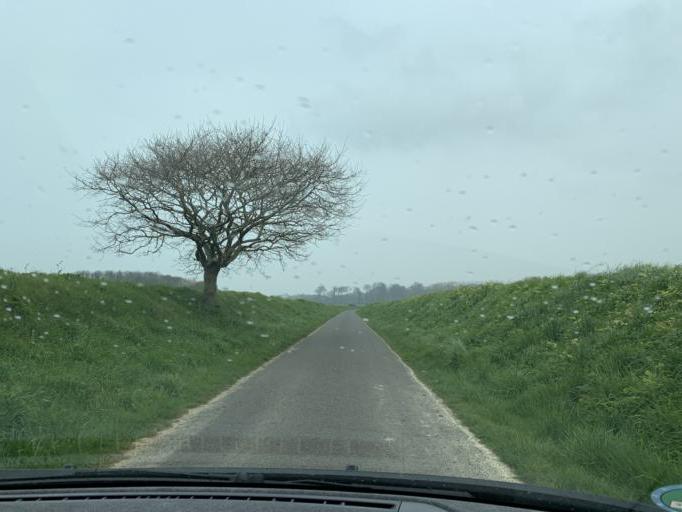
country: FR
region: Haute-Normandie
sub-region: Departement de la Seine-Maritime
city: Fontaine-le-Dun
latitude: 49.8586
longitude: 0.8345
